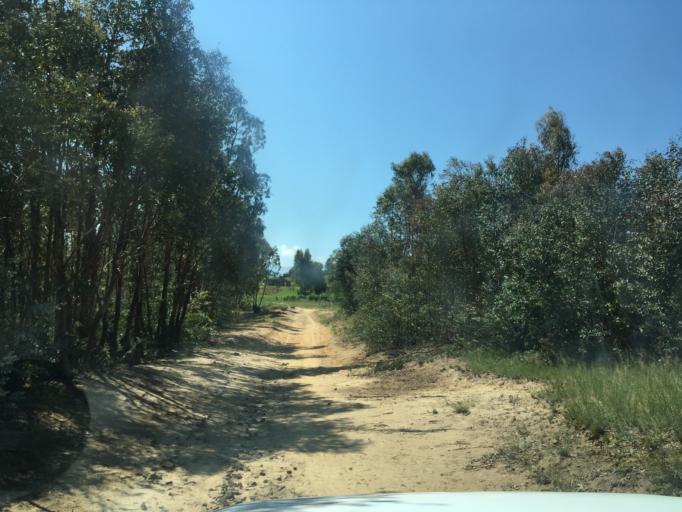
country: LS
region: Butha-Buthe
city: Butha-Buthe
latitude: -28.7253
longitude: 28.3620
